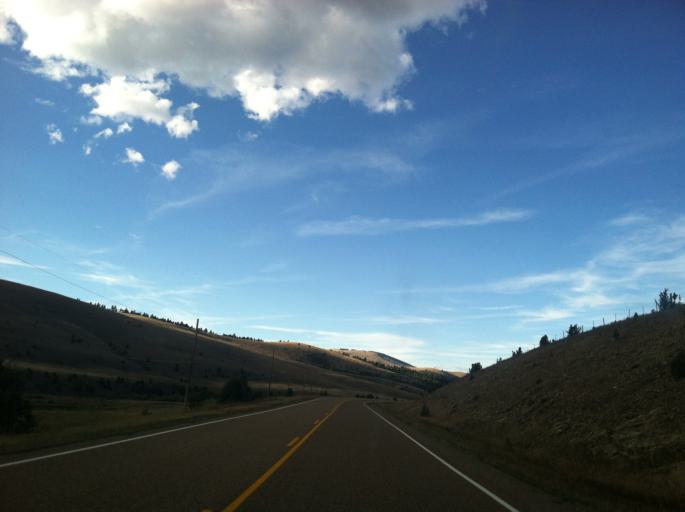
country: US
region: Montana
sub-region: Granite County
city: Philipsburg
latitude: 46.3801
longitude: -113.3131
